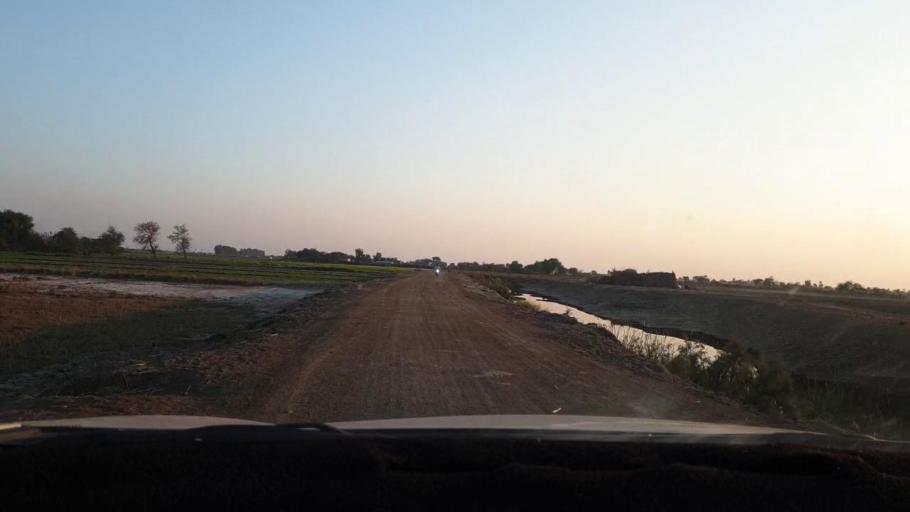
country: PK
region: Sindh
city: Berani
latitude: 25.7879
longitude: 68.8218
